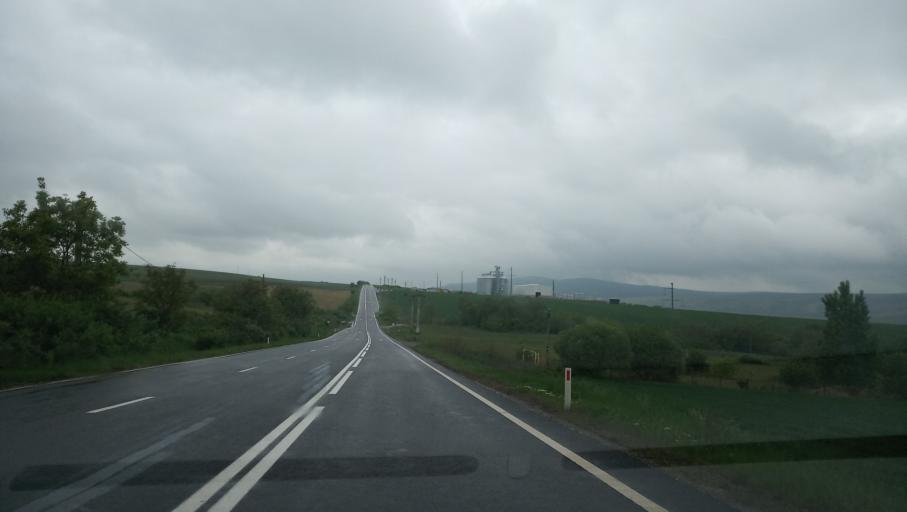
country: RO
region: Alba
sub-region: Comuna Cut
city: Cut
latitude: 45.9171
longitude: 23.7140
